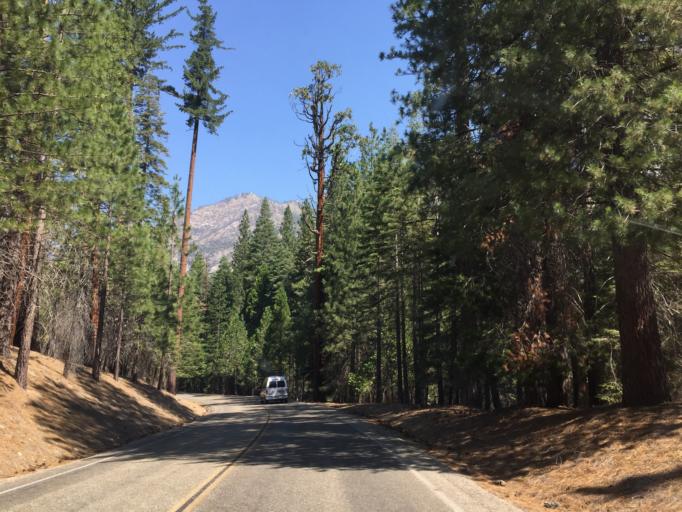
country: US
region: California
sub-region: Tulare County
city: Three Rivers
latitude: 36.7928
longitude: -118.6817
